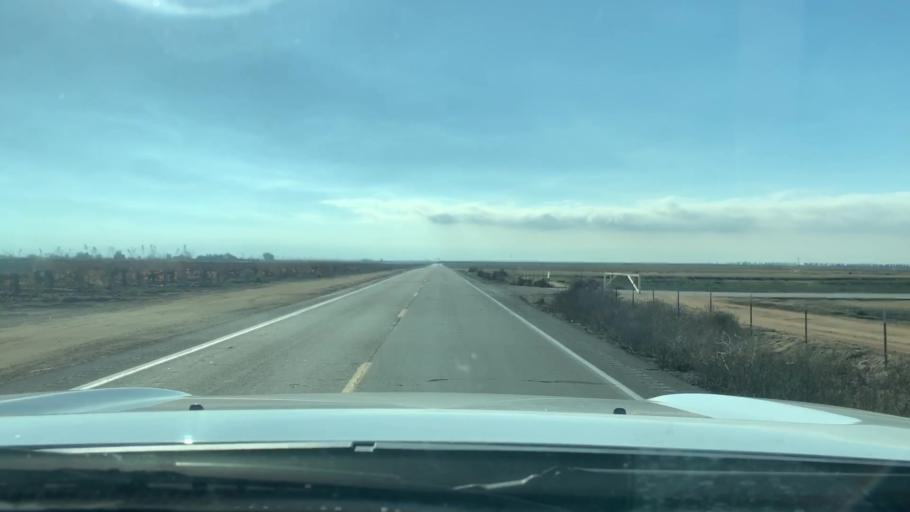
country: US
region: California
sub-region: Kern County
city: Rosedale
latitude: 35.4577
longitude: -119.1539
